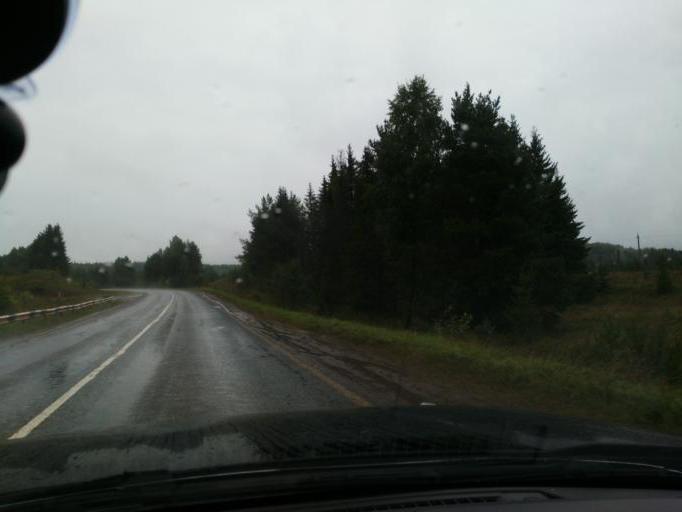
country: RU
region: Perm
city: Yugo-Kamskiy
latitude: 57.5714
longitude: 55.6826
